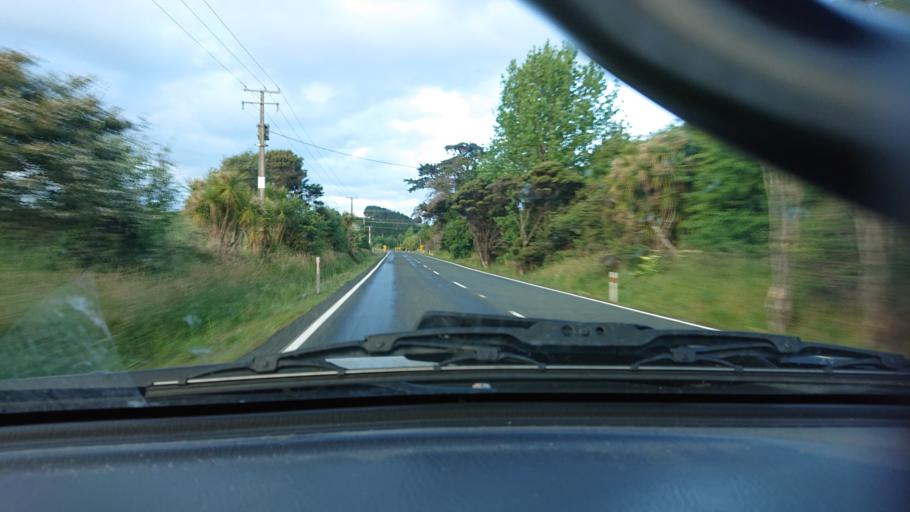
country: NZ
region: Auckland
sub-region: Auckland
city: Parakai
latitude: -36.4860
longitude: 174.4494
